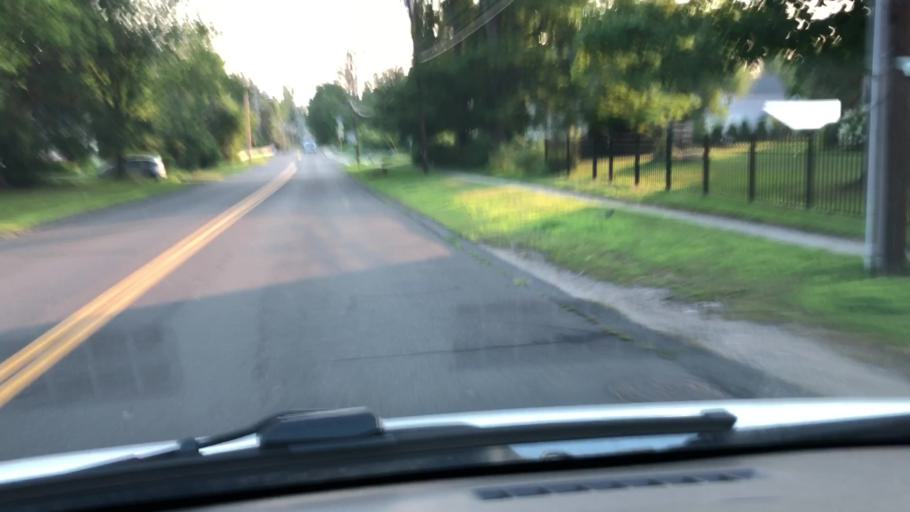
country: US
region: Massachusetts
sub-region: Hampshire County
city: Easthampton
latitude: 42.2610
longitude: -72.6777
